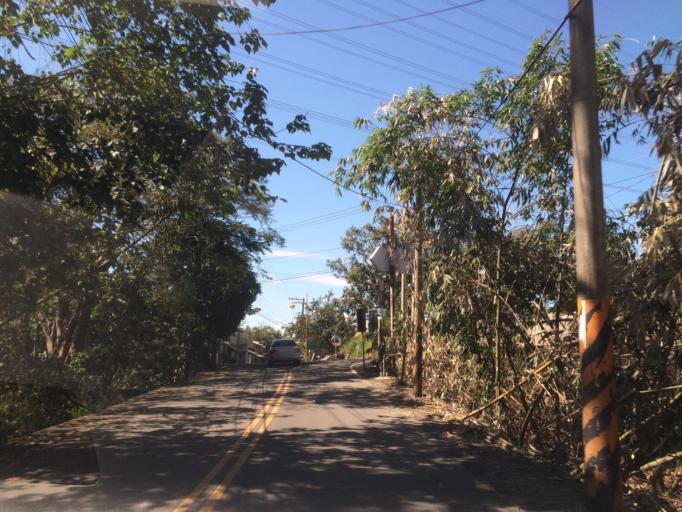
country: TW
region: Taiwan
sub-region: Yunlin
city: Douliu
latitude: 23.7013
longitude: 120.6059
